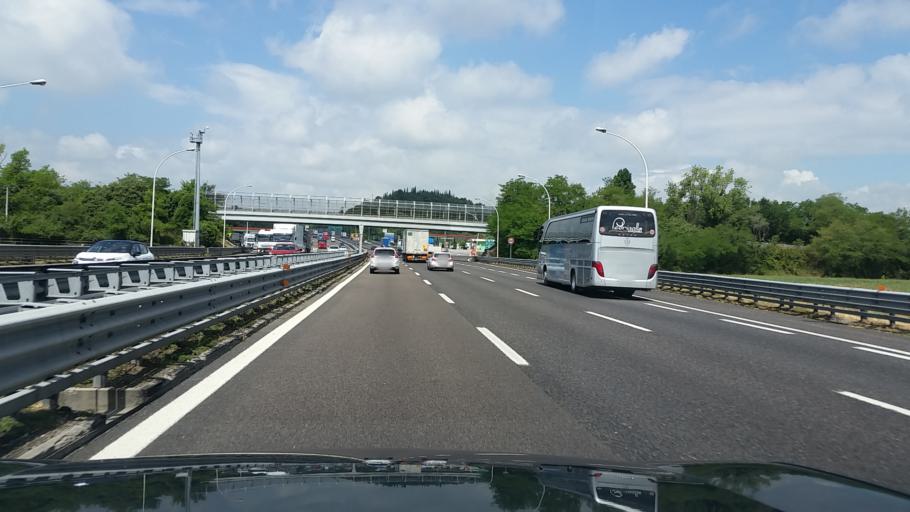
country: IT
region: Lombardy
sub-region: Provincia di Brescia
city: Desenzano del Garda
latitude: 45.4473
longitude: 10.5328
